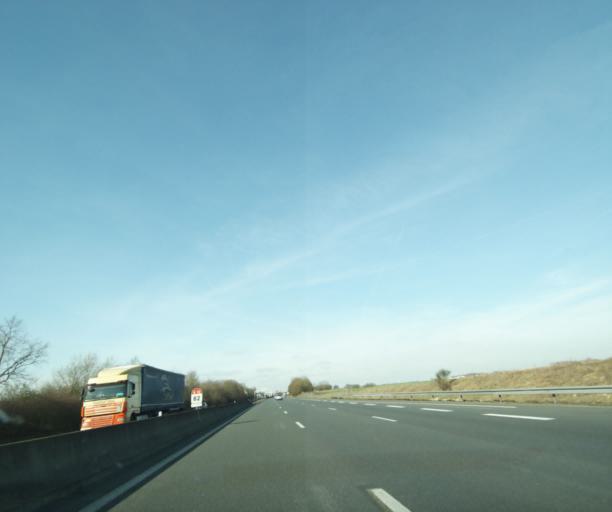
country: FR
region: Centre
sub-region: Departement du Loiret
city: Chevilly
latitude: 48.0493
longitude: 1.8416
